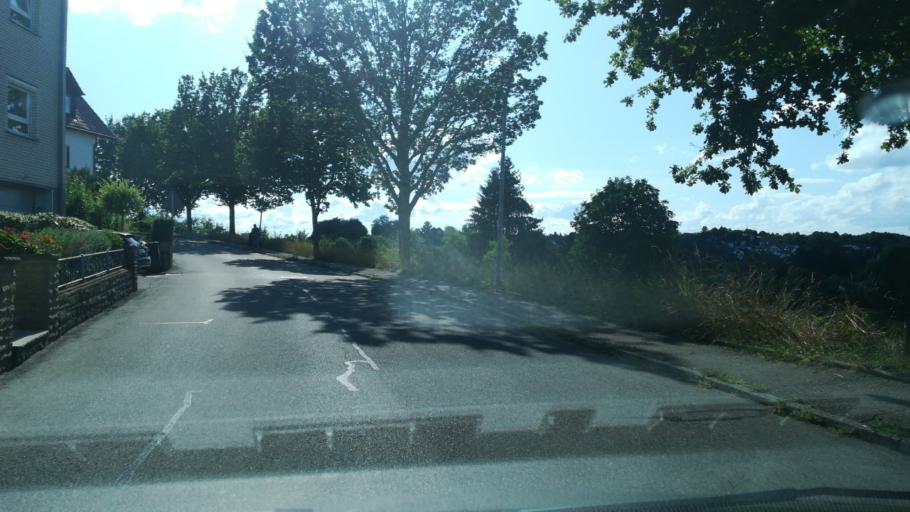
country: DE
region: Baden-Wuerttemberg
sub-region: Tuebingen Region
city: Sickenhausen
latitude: 48.5319
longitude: 9.1969
